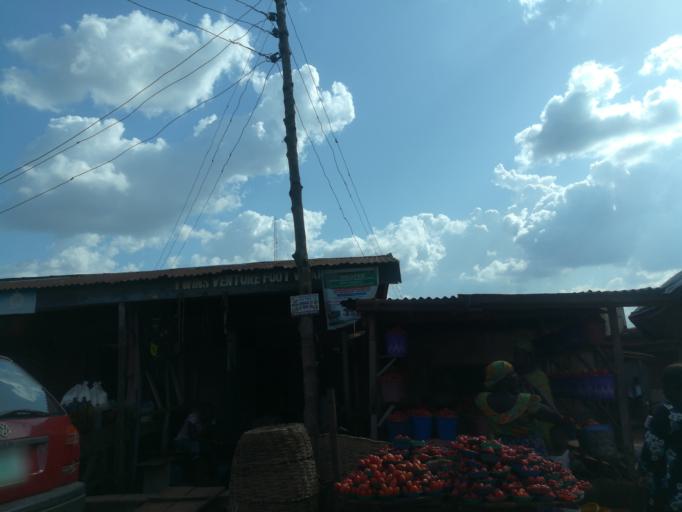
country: NG
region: Oyo
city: Ibadan
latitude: 7.4221
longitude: 3.9744
